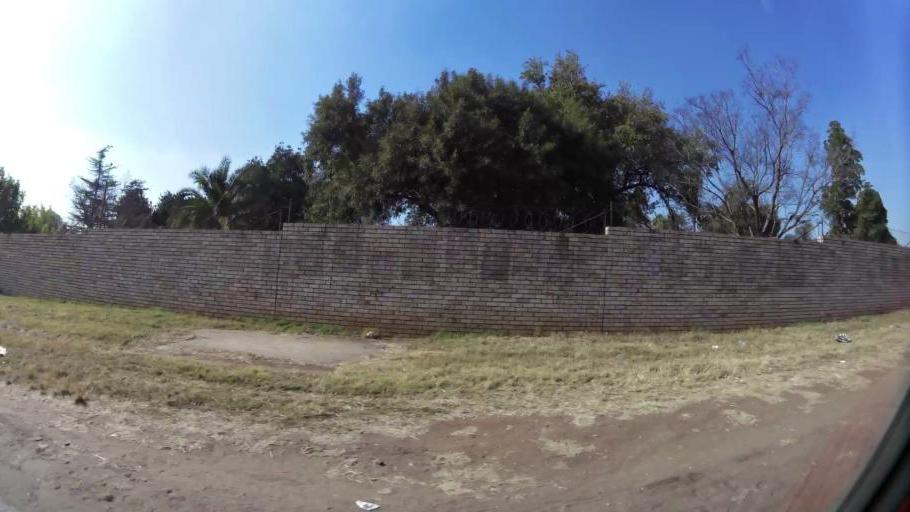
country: ZA
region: North-West
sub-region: Bojanala Platinum District Municipality
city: Rustenburg
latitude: -25.6555
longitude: 27.2415
